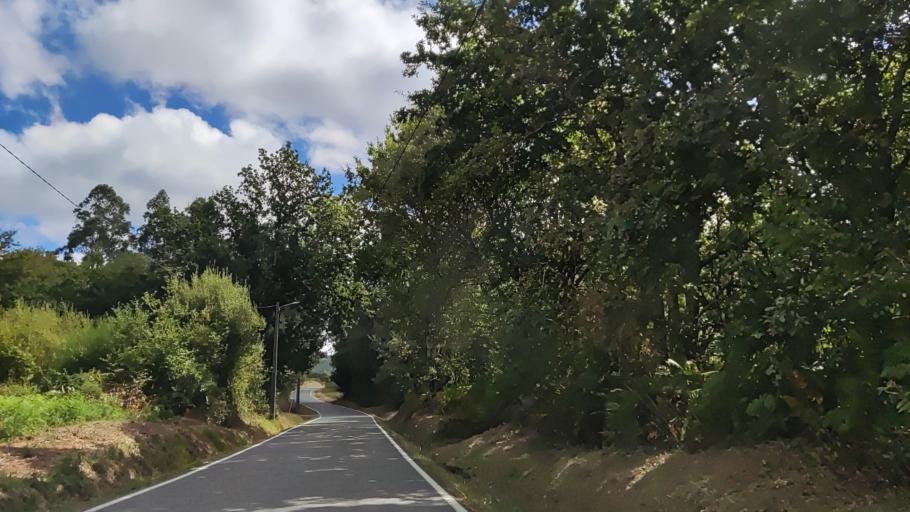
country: ES
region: Galicia
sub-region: Provincia da Coruna
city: Padron
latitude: 42.7821
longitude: -8.6624
